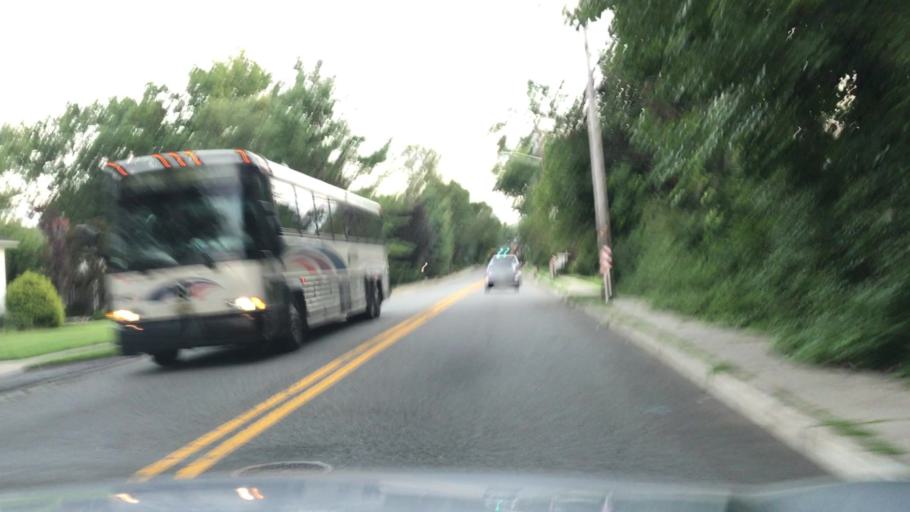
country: US
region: New Jersey
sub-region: Bergen County
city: Haworth
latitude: 40.9632
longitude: -73.9835
